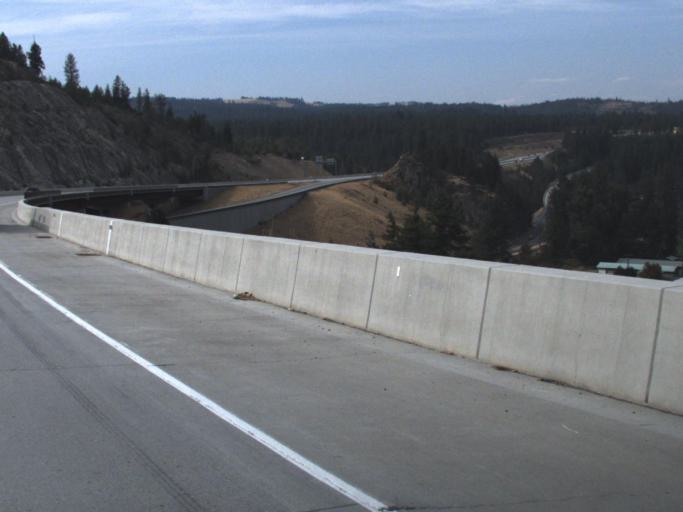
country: US
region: Washington
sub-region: Spokane County
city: Fairwood
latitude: 47.7793
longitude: -117.3990
